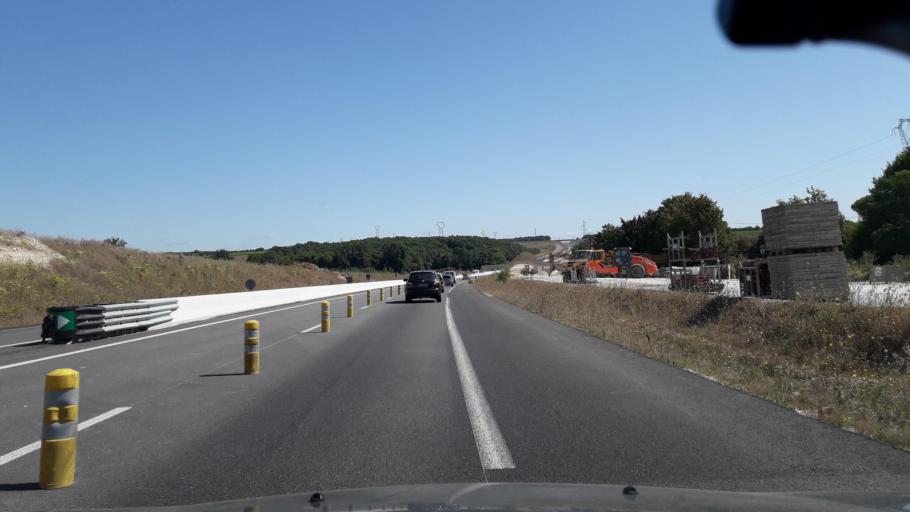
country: FR
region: Poitou-Charentes
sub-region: Departement de la Charente
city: Saint-Saturnin
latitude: 45.6757
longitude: 0.0480
